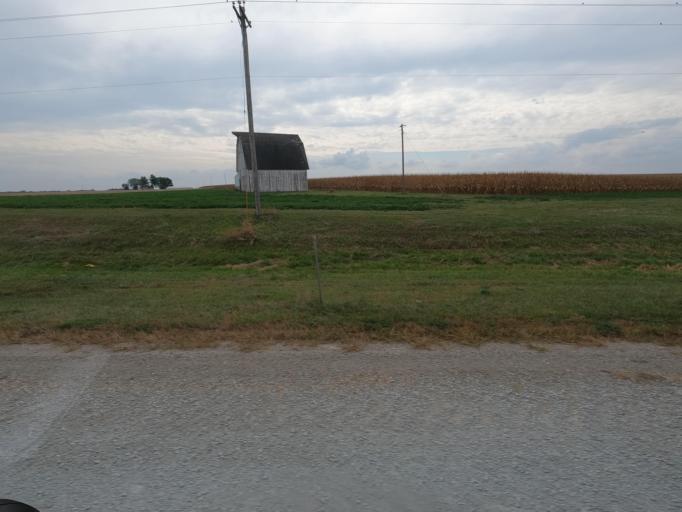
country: US
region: Iowa
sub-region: Marion County
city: Pella
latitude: 41.4414
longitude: -93.0096
